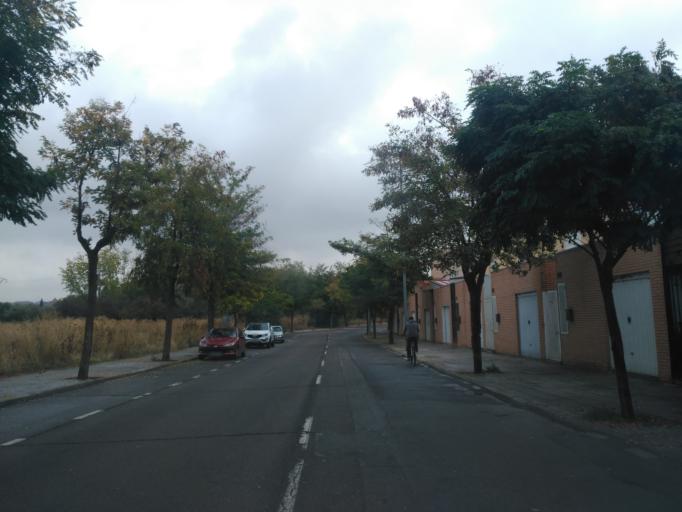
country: ES
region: Castille and Leon
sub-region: Provincia de Salamanca
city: Salamanca
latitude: 40.9578
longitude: -5.6885
